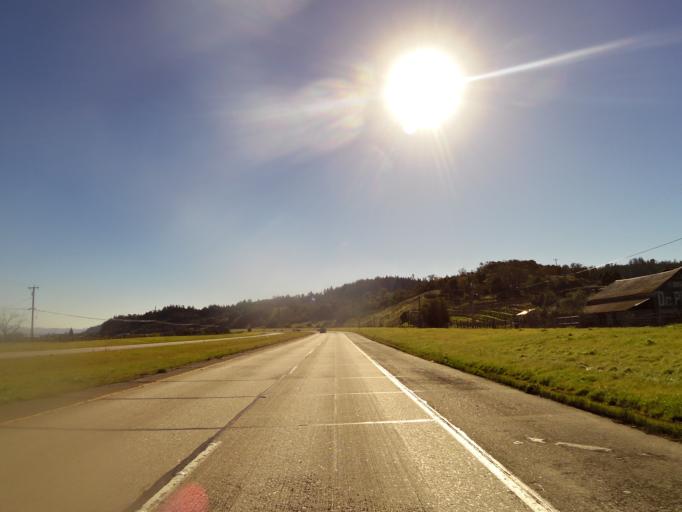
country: US
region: California
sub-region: Sonoma County
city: Cloverdale
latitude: 38.7331
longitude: -122.9441
